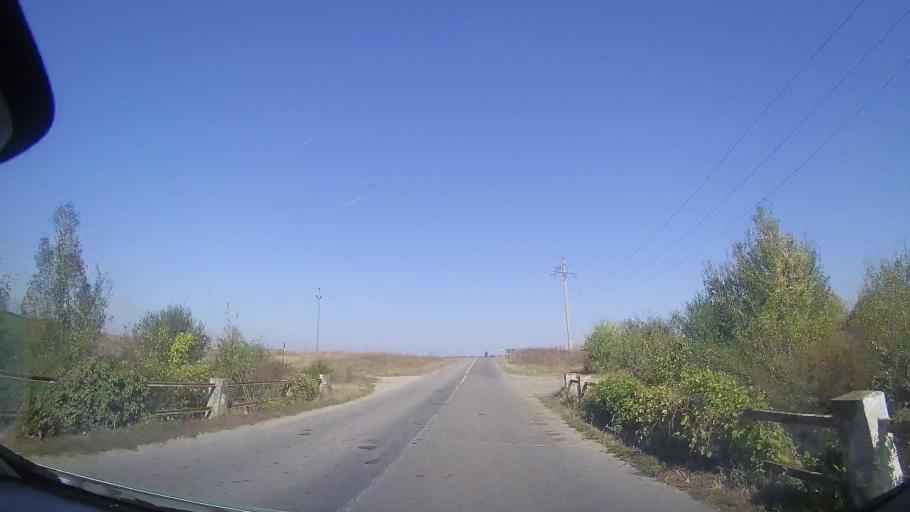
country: RO
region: Timis
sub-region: Comuna Costeiu
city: Costeiu
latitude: 45.7477
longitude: 21.8469
